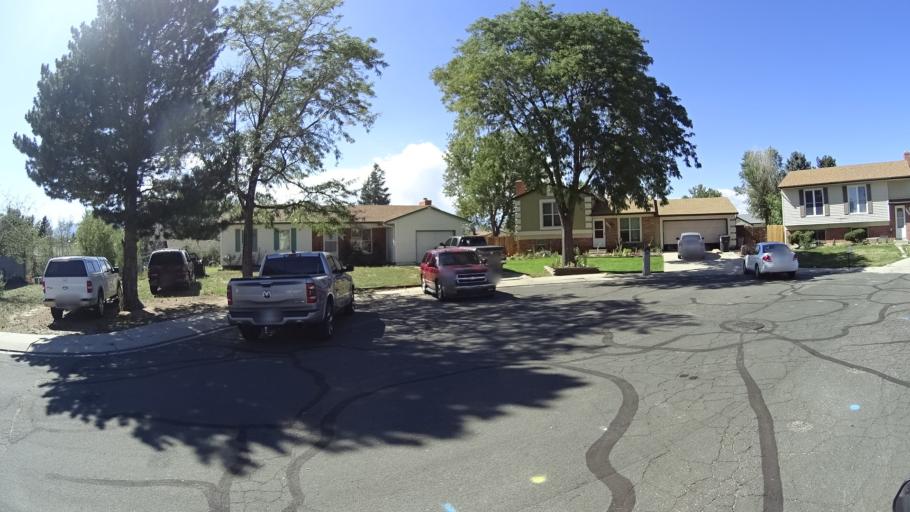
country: US
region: Colorado
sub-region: El Paso County
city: Stratmoor
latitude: 38.7935
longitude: -104.7403
